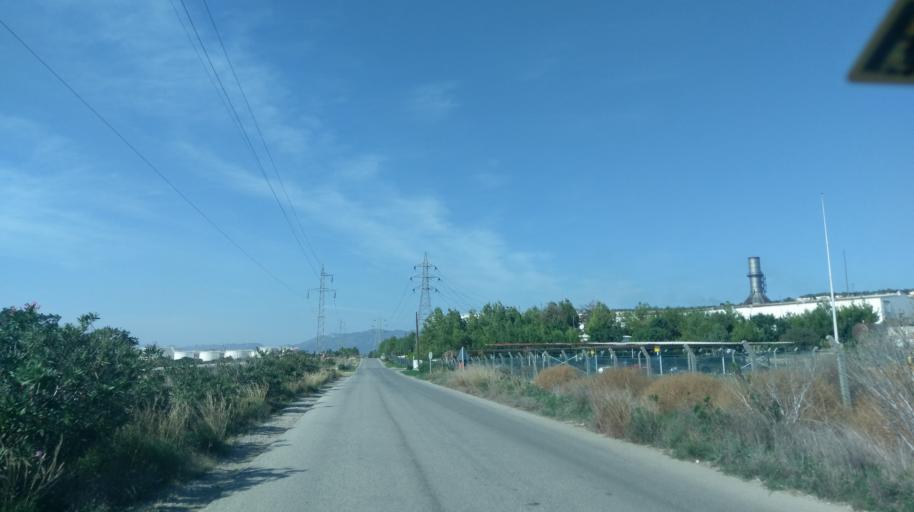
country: CY
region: Ammochostos
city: Trikomo
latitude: 35.3278
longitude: 33.9996
